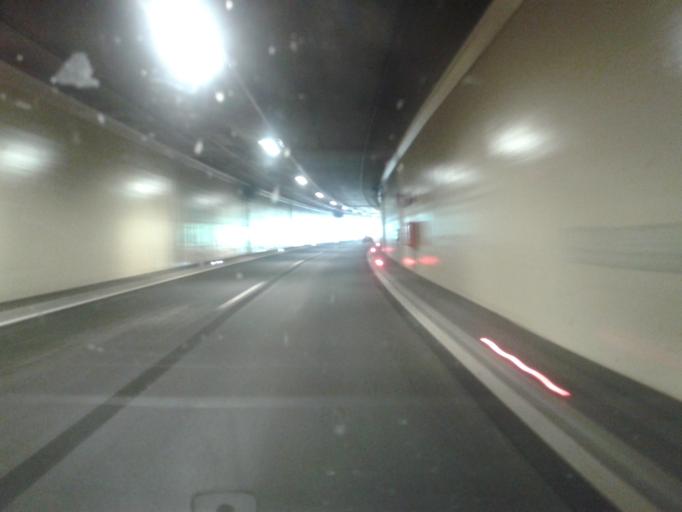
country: AT
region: Carinthia
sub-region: Klagenfurt am Woerthersee
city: Klagenfurt am Woerthersee
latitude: 46.6558
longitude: 14.2781
